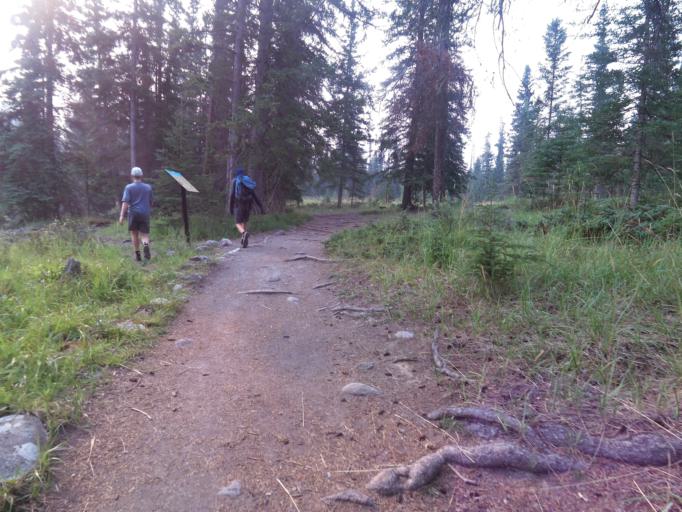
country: CA
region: Alberta
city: Jasper Park Lodge
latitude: 52.8785
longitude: -118.0611
